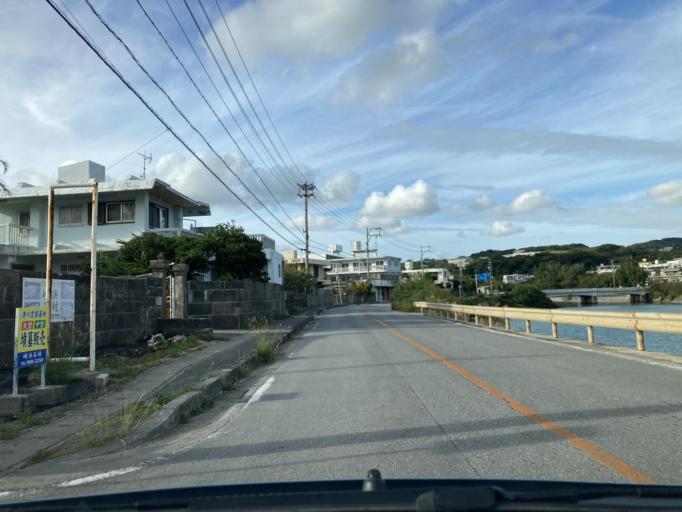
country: JP
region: Okinawa
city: Itoman
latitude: 26.1299
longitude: 127.7599
